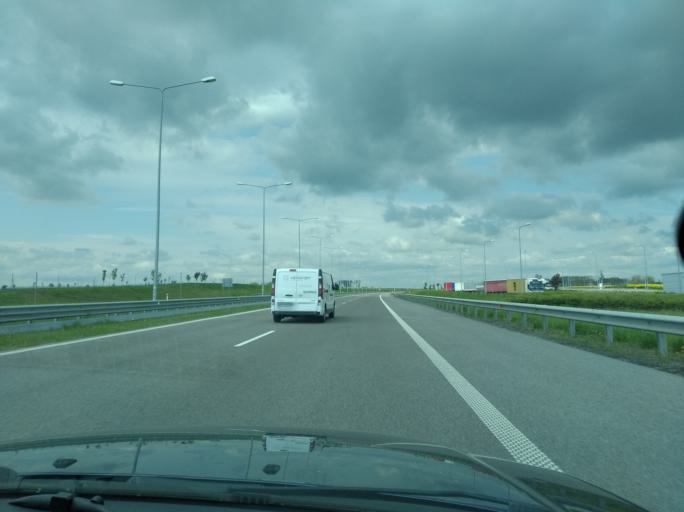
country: PL
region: Subcarpathian Voivodeship
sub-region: Powiat jaroslawski
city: Ostrow
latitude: 49.9170
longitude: 22.7569
